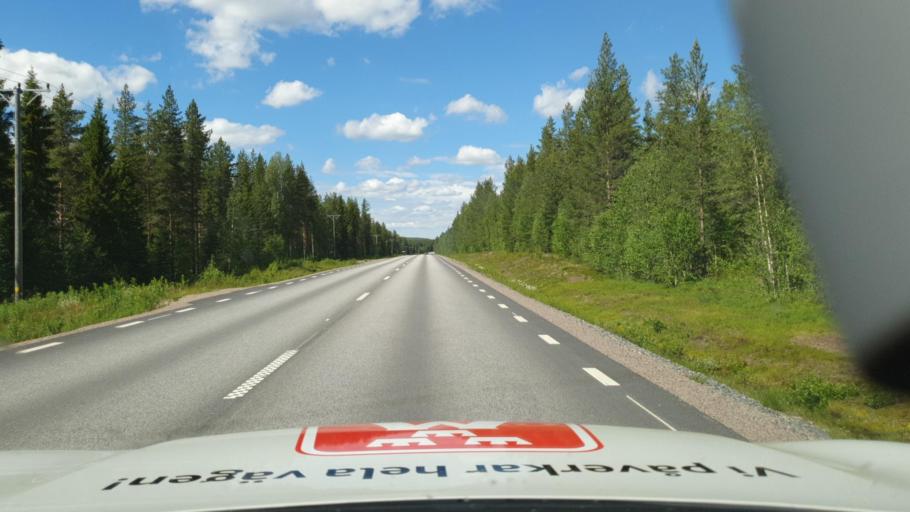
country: SE
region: Vaesterbotten
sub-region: Skelleftea Kommun
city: Boliden
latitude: 64.9360
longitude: 20.2932
